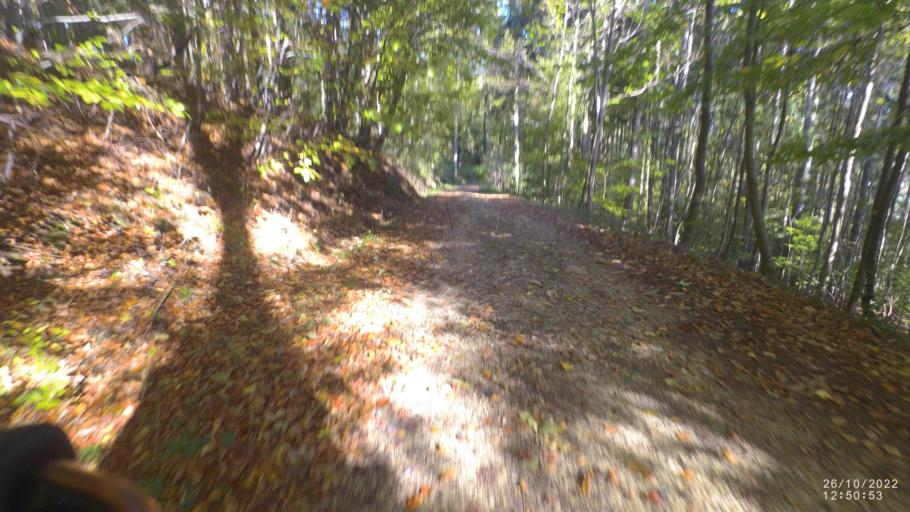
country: DE
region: Baden-Wuerttemberg
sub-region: Regierungsbezirk Stuttgart
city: Schlat
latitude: 48.6480
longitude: 9.6894
